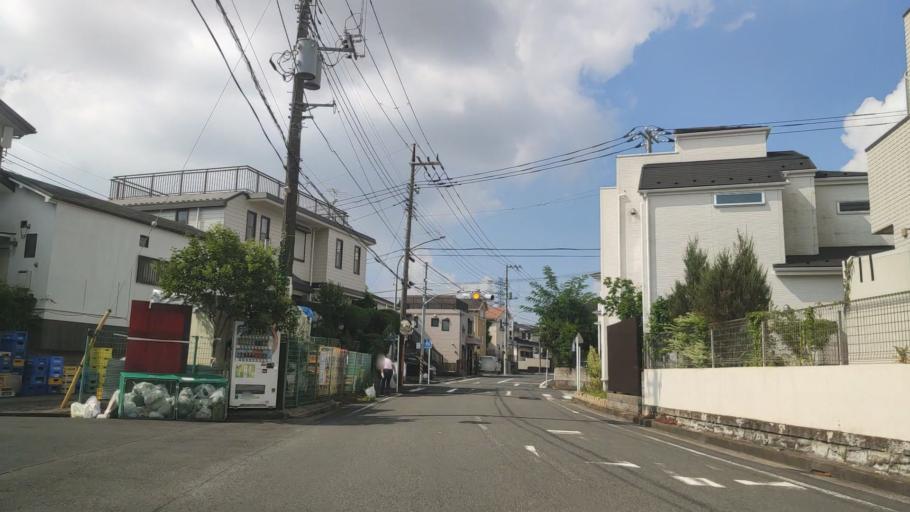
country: JP
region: Kanagawa
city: Yokohama
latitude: 35.4009
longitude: 139.5644
